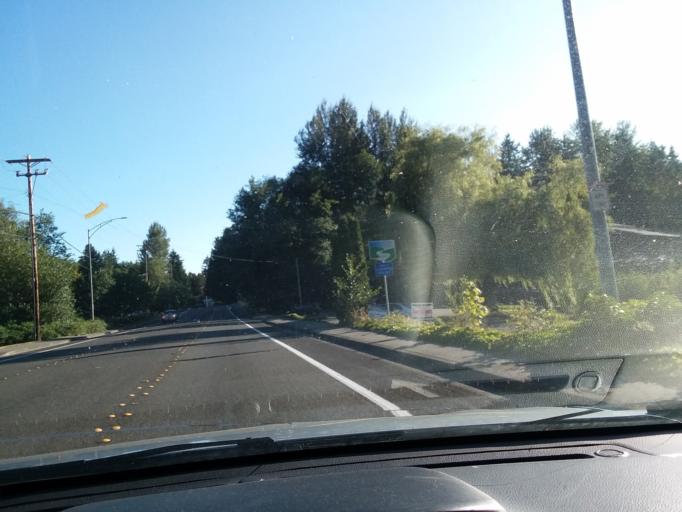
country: US
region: Washington
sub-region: Snohomish County
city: Lynnwood
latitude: 47.8162
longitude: -122.3016
